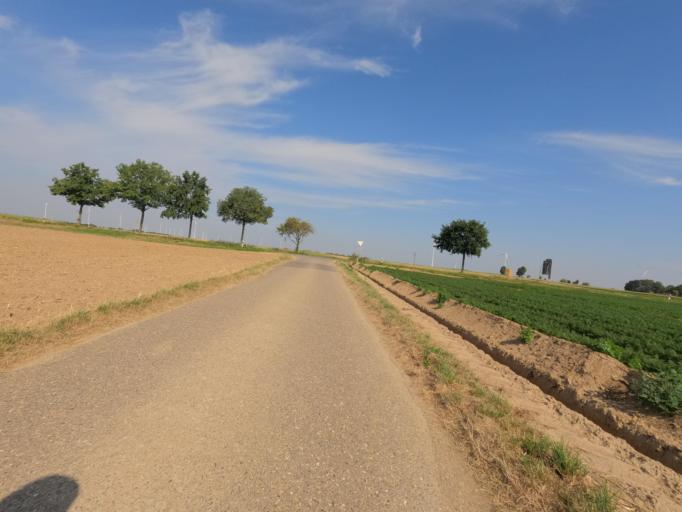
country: DE
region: North Rhine-Westphalia
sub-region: Regierungsbezirk Koln
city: Linnich
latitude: 50.9957
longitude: 6.3392
